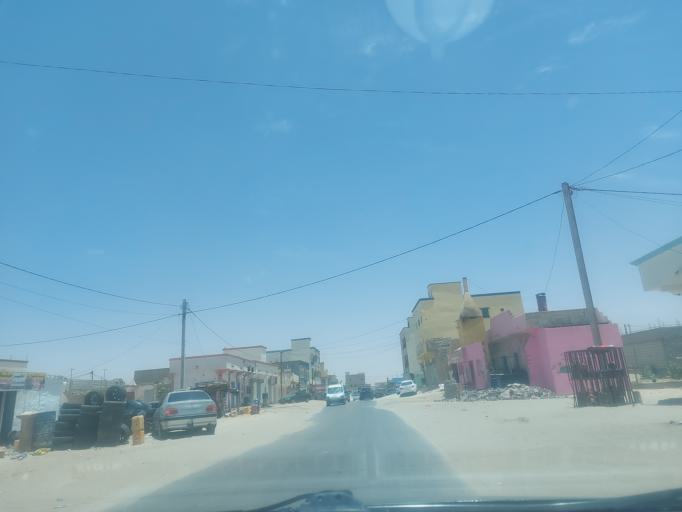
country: MR
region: Nouakchott
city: Nouakchott
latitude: 18.0685
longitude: -15.9460
